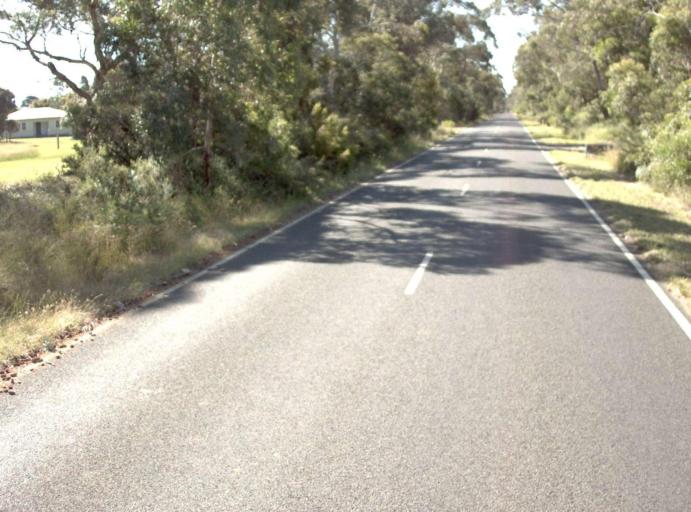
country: AU
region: Victoria
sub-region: Latrobe
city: Traralgon
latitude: -38.6639
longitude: 146.6867
